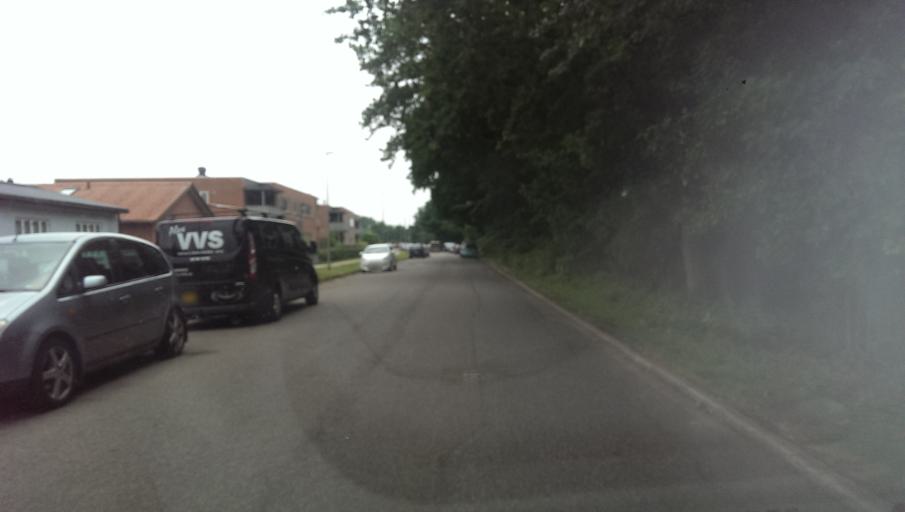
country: DK
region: South Denmark
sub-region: Esbjerg Kommune
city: Esbjerg
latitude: 55.4649
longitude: 8.4713
